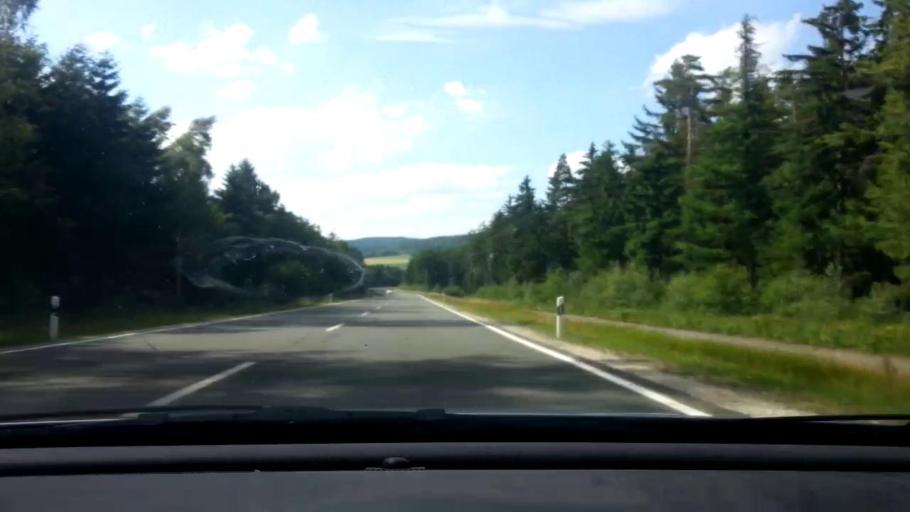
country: DE
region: Bavaria
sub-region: Upper Palatinate
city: Erbendorf
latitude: 49.8424
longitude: 12.0041
